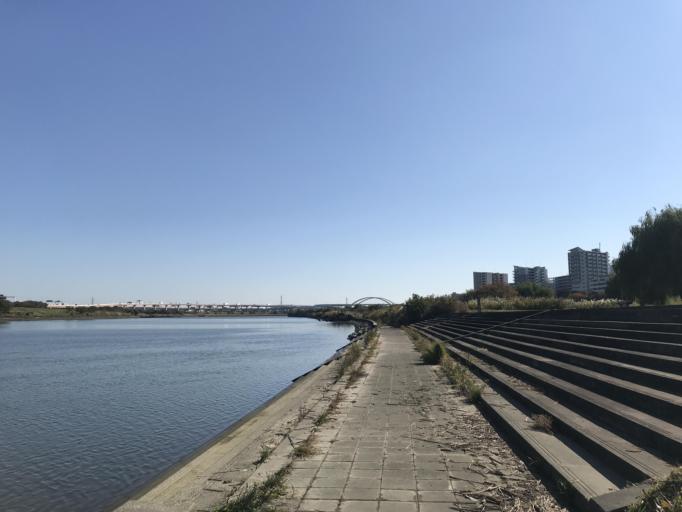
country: JP
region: Saitama
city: Kawaguchi
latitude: 35.7743
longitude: 139.7464
